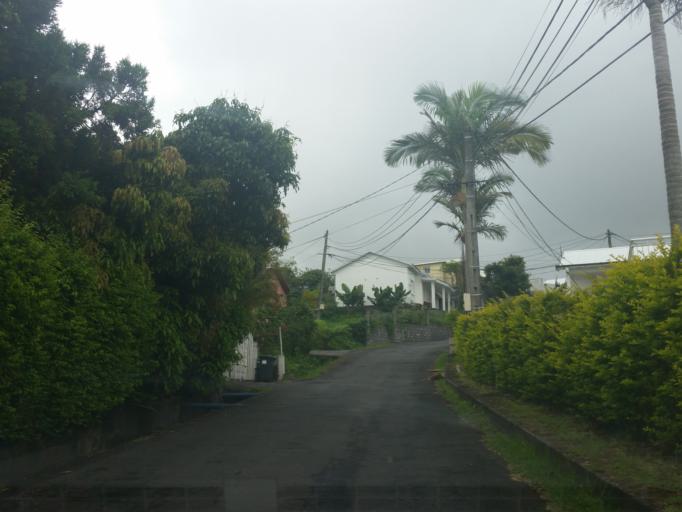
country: RE
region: Reunion
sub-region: Reunion
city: Le Tampon
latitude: -21.2369
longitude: 55.5195
